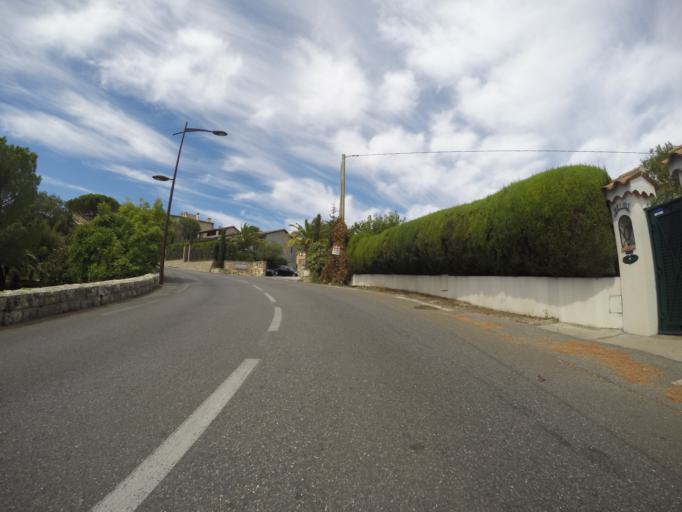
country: FR
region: Provence-Alpes-Cote d'Azur
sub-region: Departement des Alpes-Maritimes
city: Mougins
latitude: 43.6012
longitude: 6.9973
